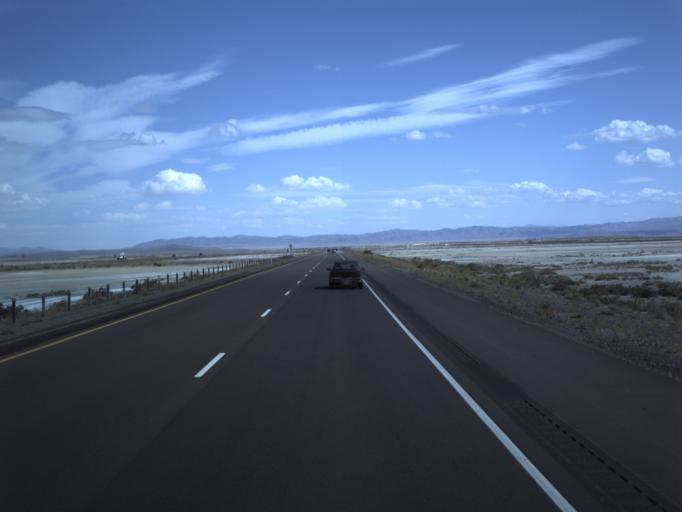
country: US
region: Utah
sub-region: Tooele County
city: Wendover
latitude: 40.7274
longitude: -113.3159
